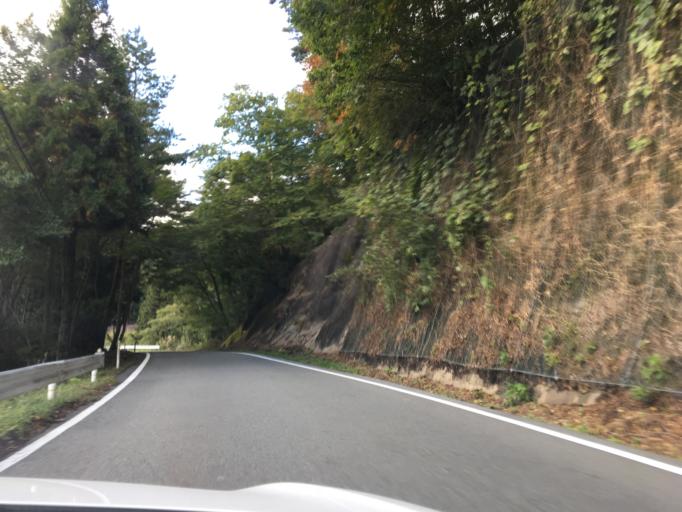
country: JP
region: Fukushima
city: Namie
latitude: 37.5605
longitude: 140.8290
